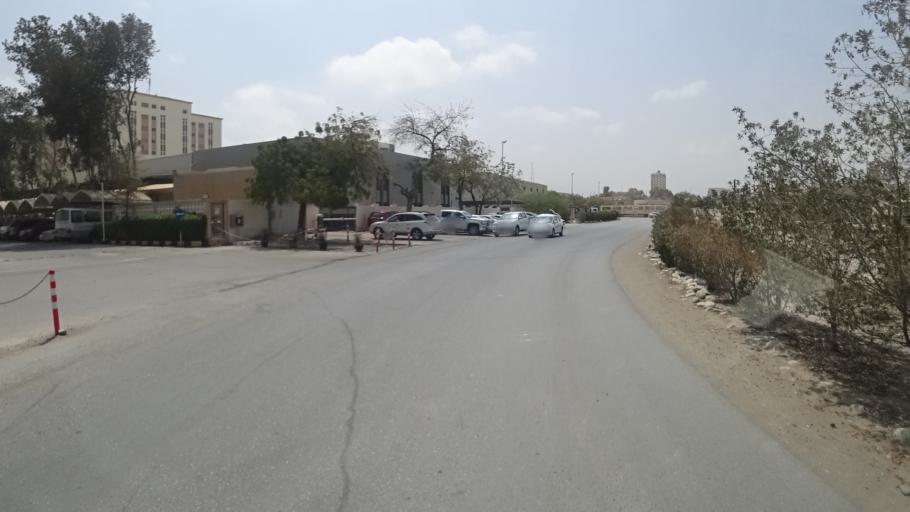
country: OM
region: Muhafazat Masqat
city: Bawshar
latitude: 23.5748
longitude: 58.3750
